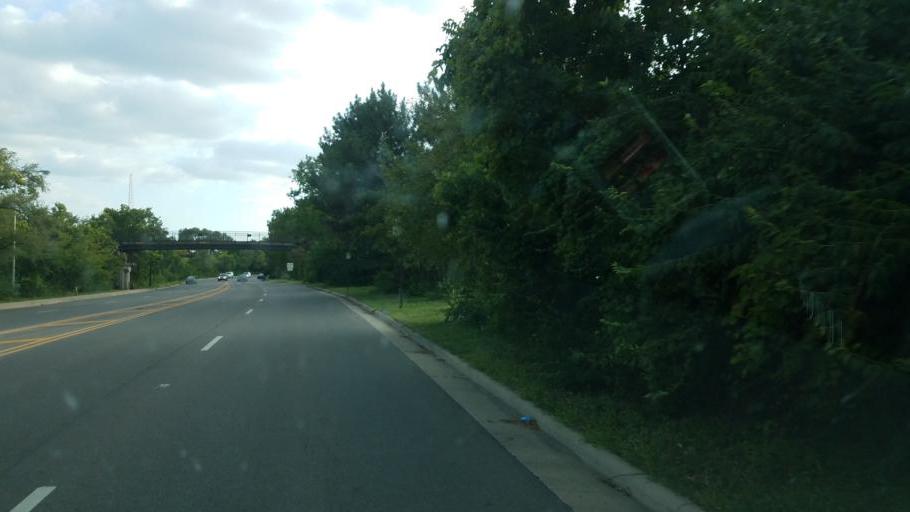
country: US
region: Ohio
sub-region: Franklin County
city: Grandview Heights
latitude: 40.0012
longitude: -83.0244
